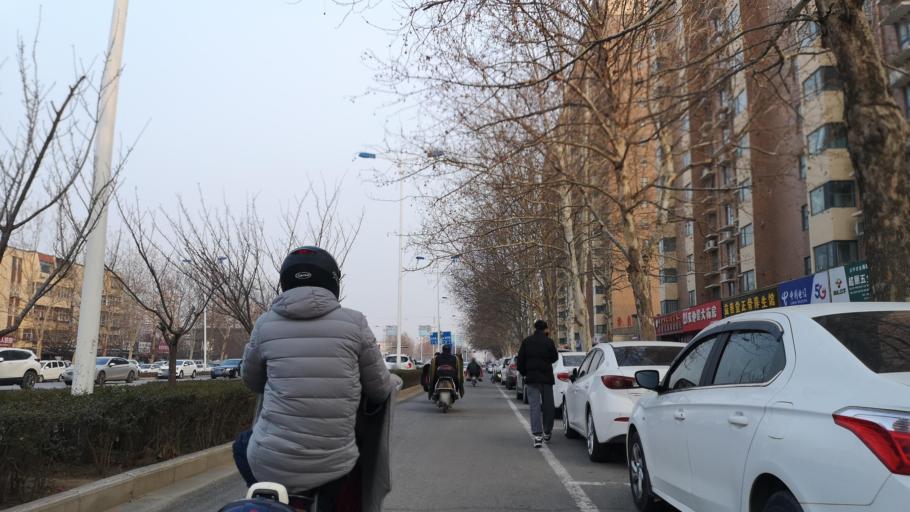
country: CN
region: Henan Sheng
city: Zhongyuanlu
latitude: 35.7649
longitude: 115.0954
